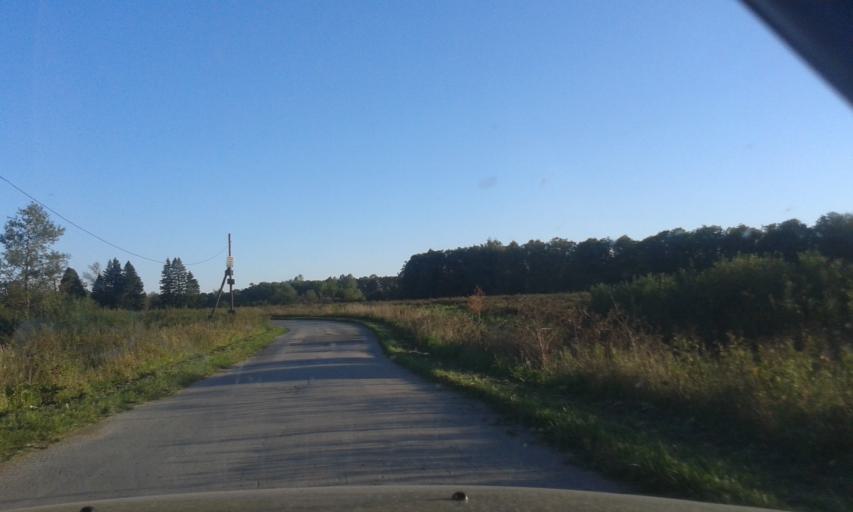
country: RU
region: Tula
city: Krapivna
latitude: 54.1170
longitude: 37.1521
